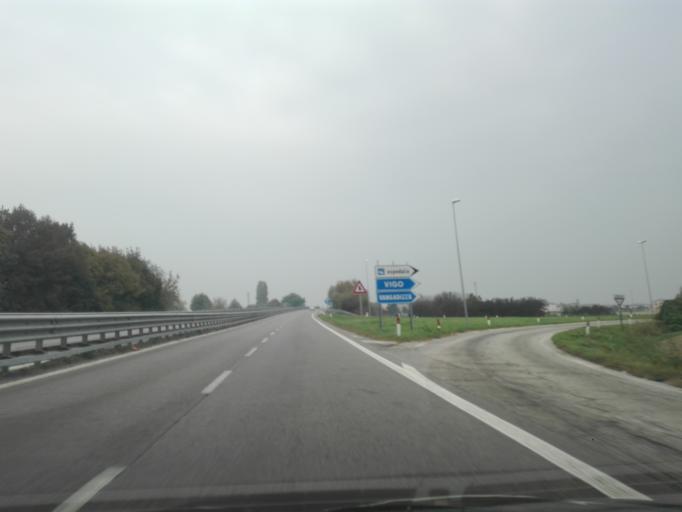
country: IT
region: Veneto
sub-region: Provincia di Verona
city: Villa Bartolomea
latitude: 45.1633
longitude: 11.3046
